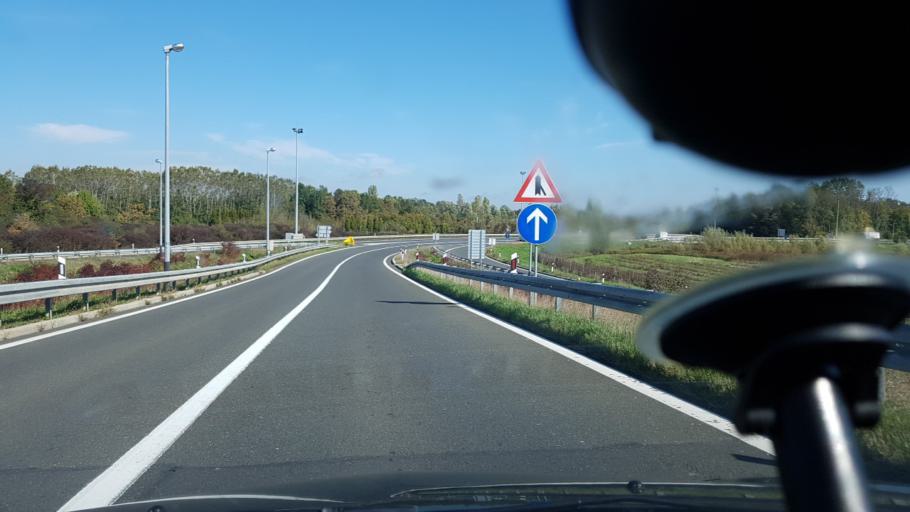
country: HR
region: Zagrebacka
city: Brckovljani
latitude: 45.7652
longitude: 16.2267
